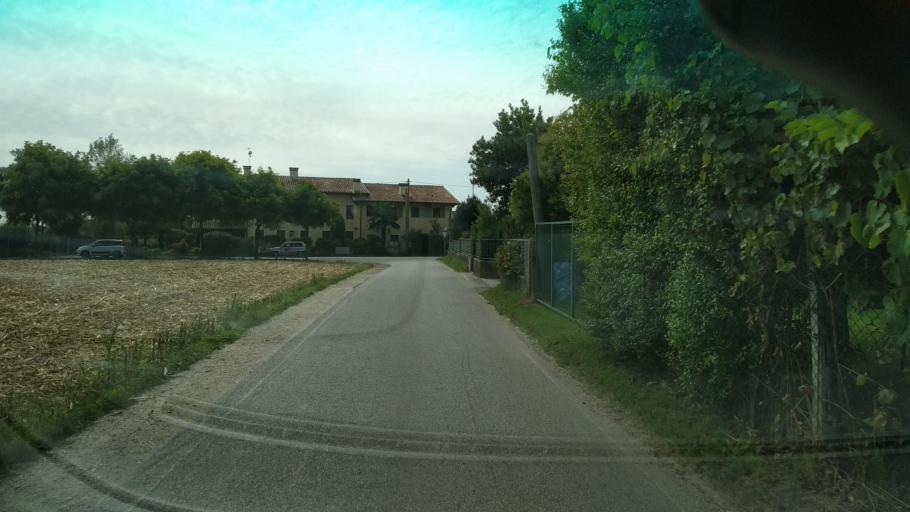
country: IT
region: Veneto
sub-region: Provincia di Vicenza
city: Sandrigo
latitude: 45.6368
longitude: 11.5974
